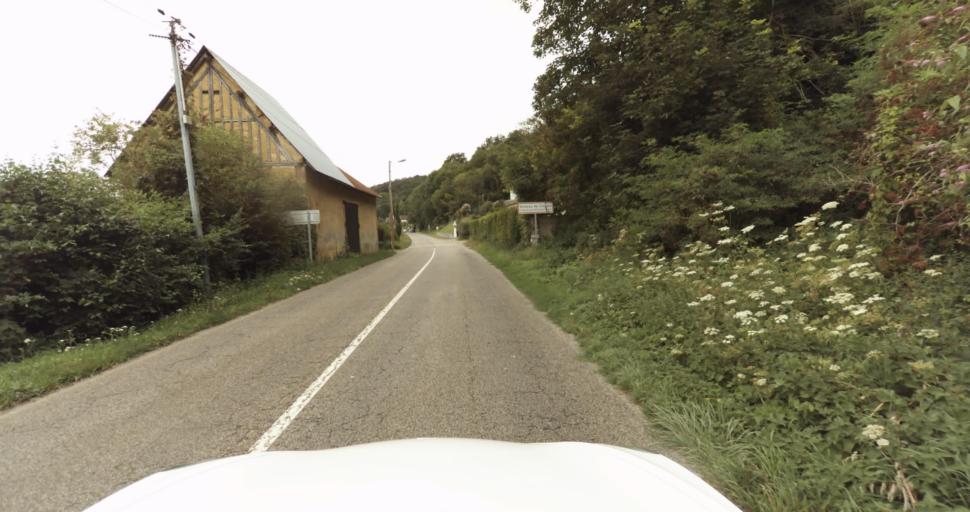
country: FR
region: Haute-Normandie
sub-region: Departement de l'Eure
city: Saint-Sebastien-de-Morsent
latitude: 48.9997
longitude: 1.0580
